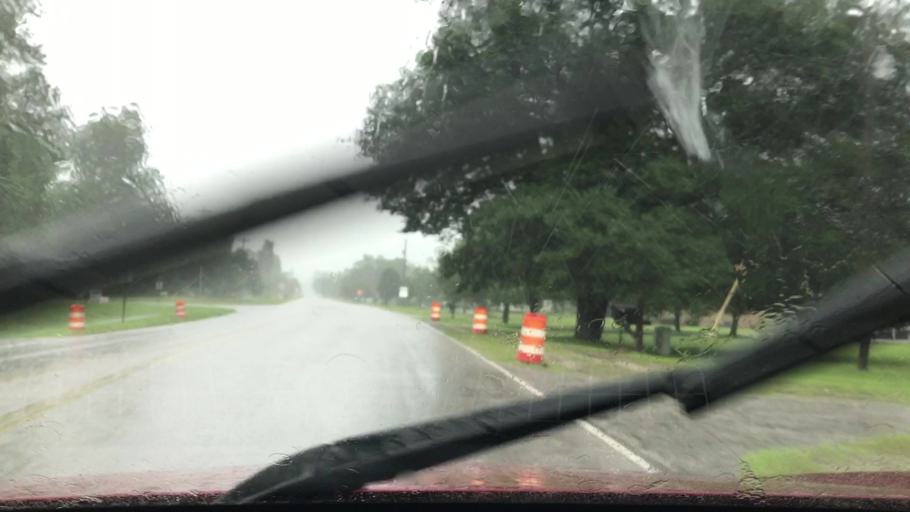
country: US
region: South Carolina
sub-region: Horry County
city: Red Hill
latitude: 33.8763
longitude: -78.9730
